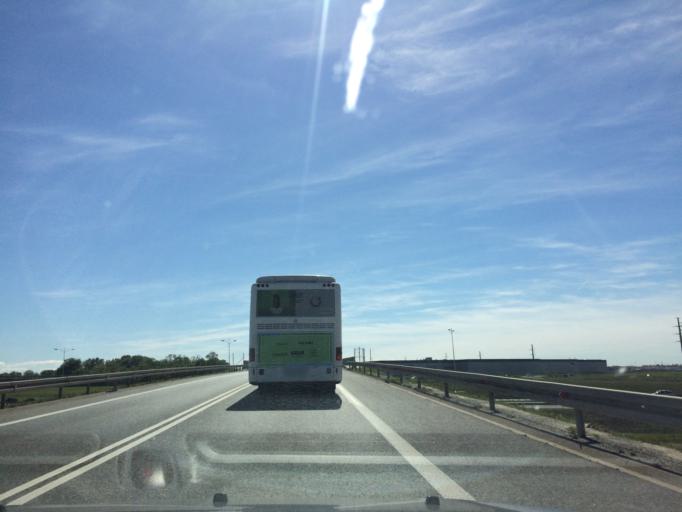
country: PL
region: Lower Silesian Voivodeship
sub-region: Powiat wroclawski
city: Tyniec Maly
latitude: 51.0365
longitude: 16.9389
